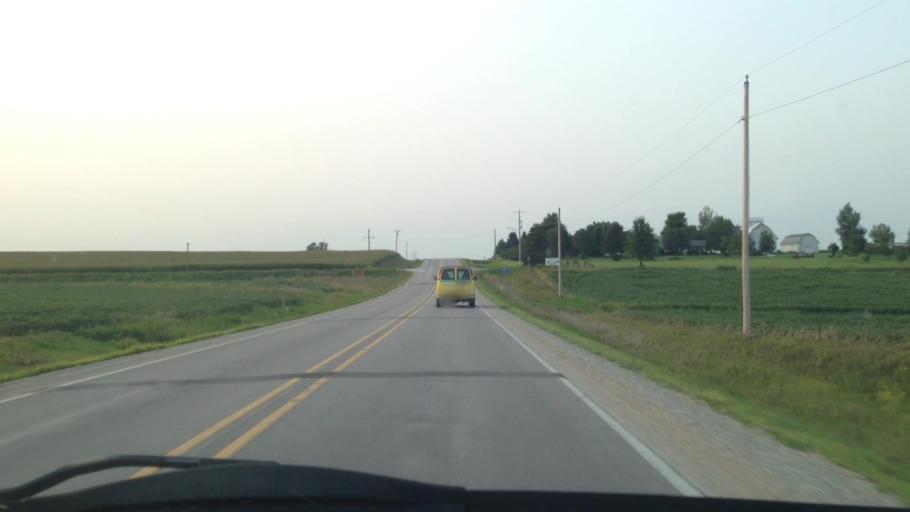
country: US
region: Iowa
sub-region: Benton County
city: Atkins
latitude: 42.0199
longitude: -91.8738
